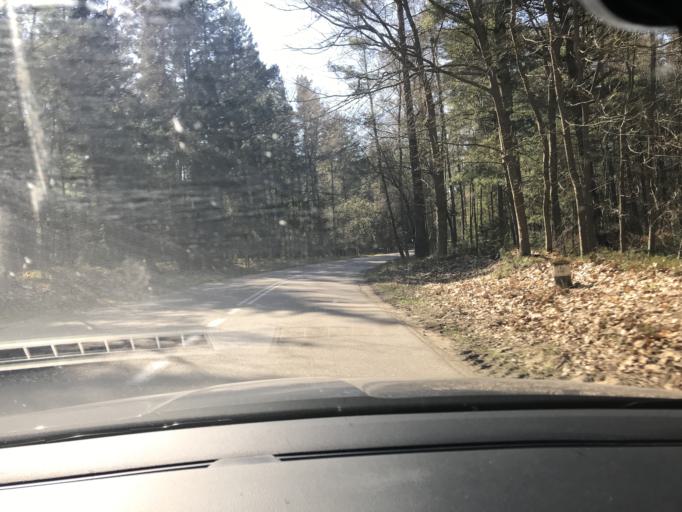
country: PL
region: Pomeranian Voivodeship
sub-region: Powiat nowodworski
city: Krynica Morska
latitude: 54.3563
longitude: 19.3264
